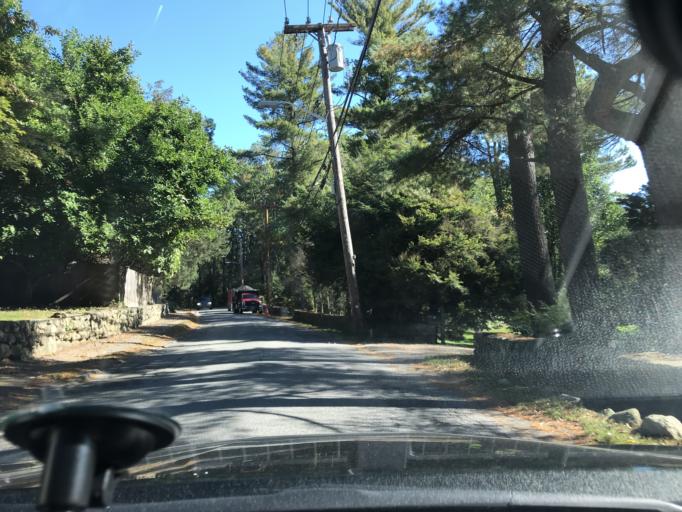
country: US
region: Massachusetts
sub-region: Norfolk County
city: Wellesley
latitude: 42.2882
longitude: -71.2838
